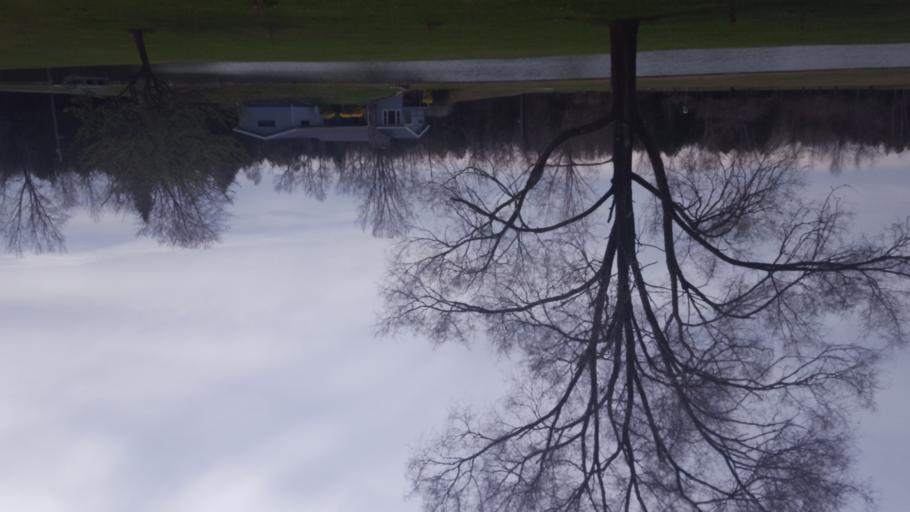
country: US
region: Michigan
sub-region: Clare County
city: Clare
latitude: 43.8727
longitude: -84.7646
